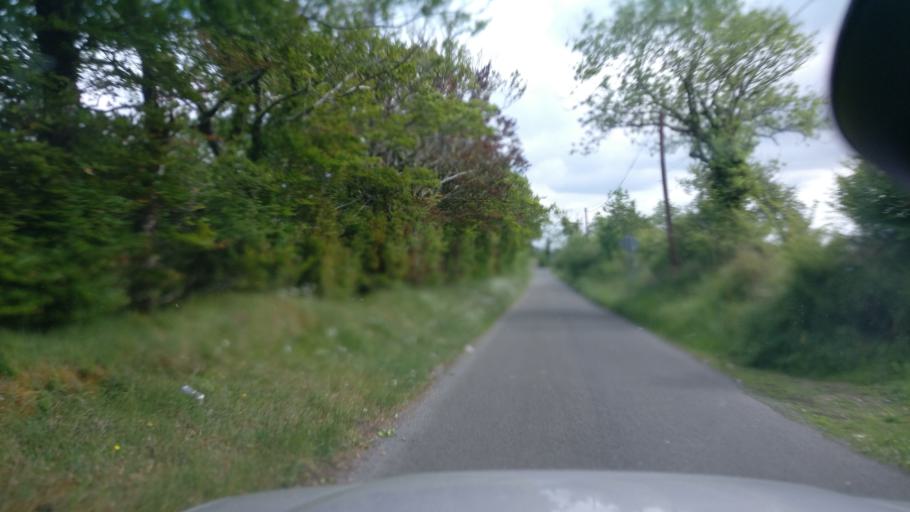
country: IE
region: Connaught
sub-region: County Galway
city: Ballinasloe
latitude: 53.2870
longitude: -8.3418
